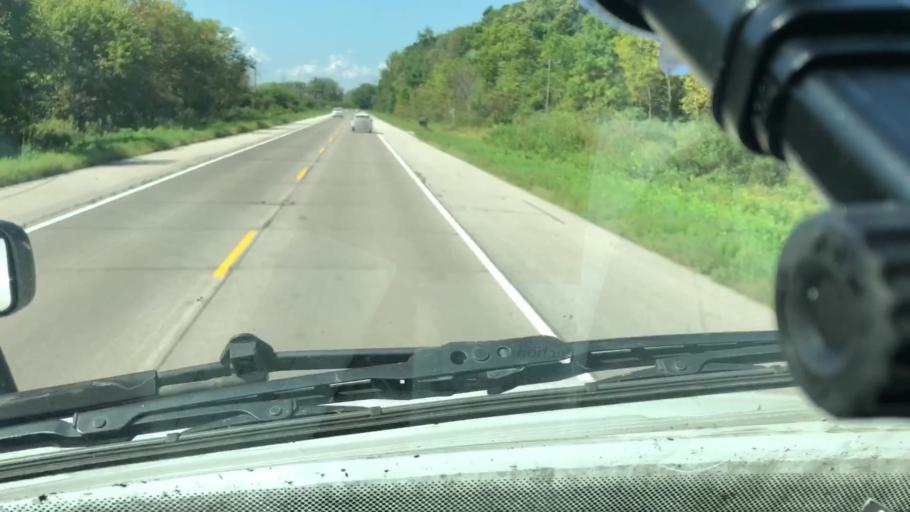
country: US
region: Minnesota
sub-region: Winona County
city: Winona
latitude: 44.0681
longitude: -91.5867
